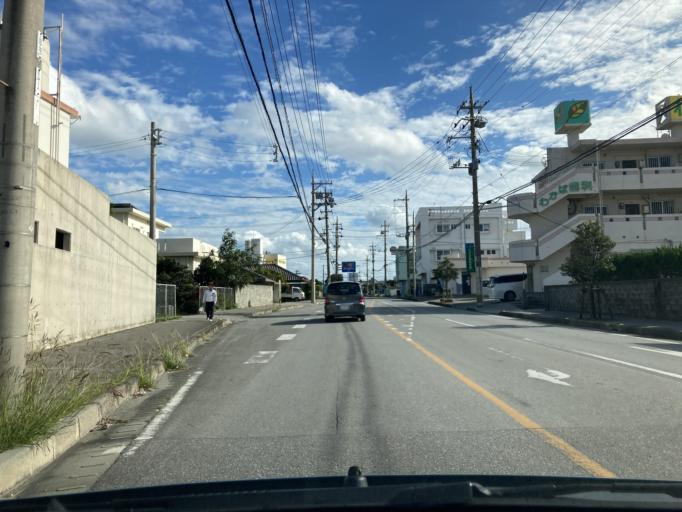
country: JP
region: Okinawa
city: Ishikawa
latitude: 26.4131
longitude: 127.8241
